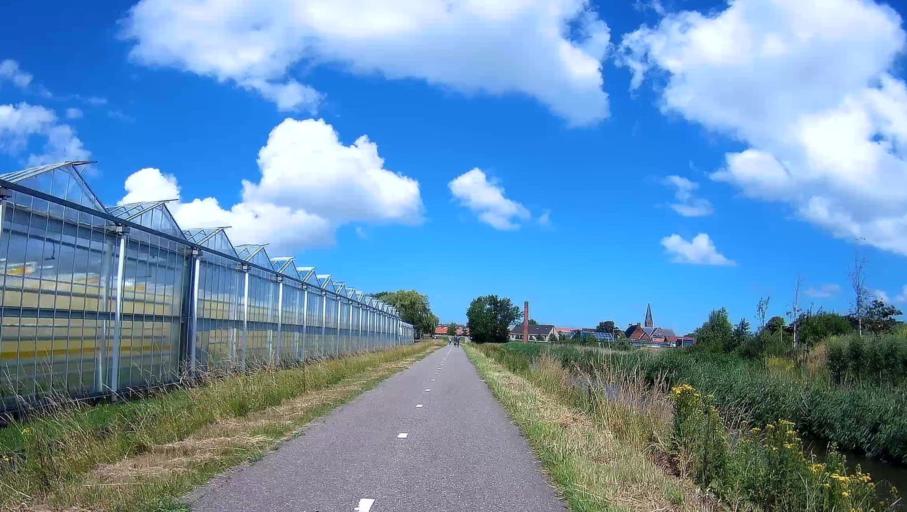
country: NL
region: South Holland
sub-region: Gemeente Westland
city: De Lier
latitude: 51.9696
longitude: 4.2536
